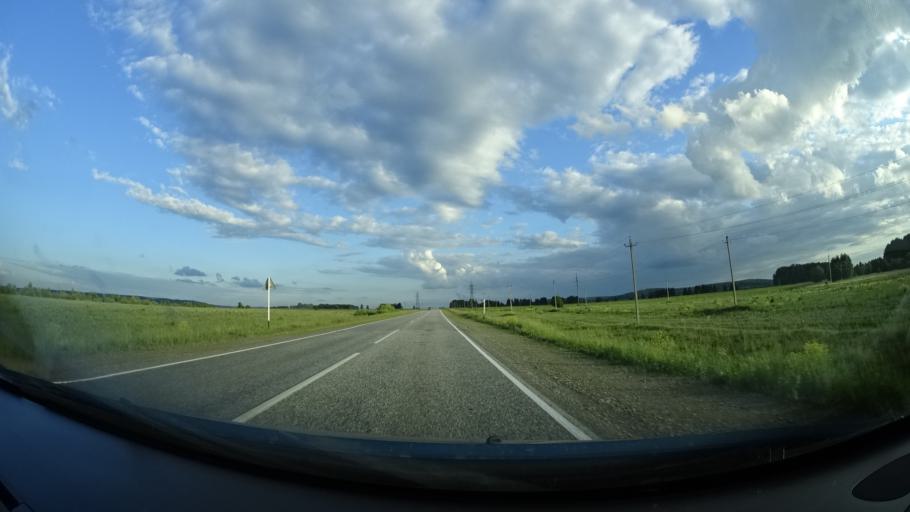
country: RU
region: Perm
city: Barda
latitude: 57.0781
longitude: 55.5428
